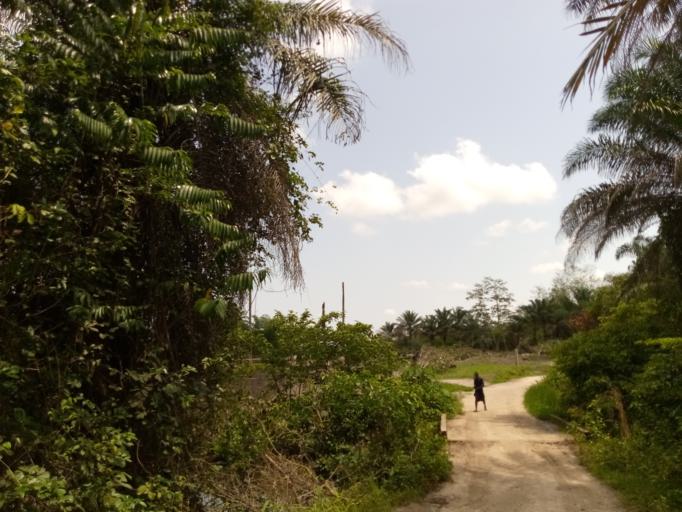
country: SL
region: Western Area
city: Waterloo
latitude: 8.3666
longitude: -13.0026
